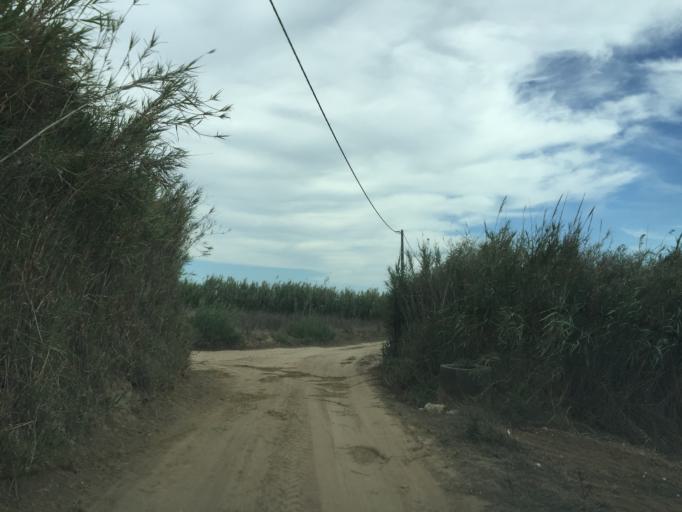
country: PT
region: Lisbon
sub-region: Lourinha
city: Lourinha
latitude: 39.1890
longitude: -9.3438
